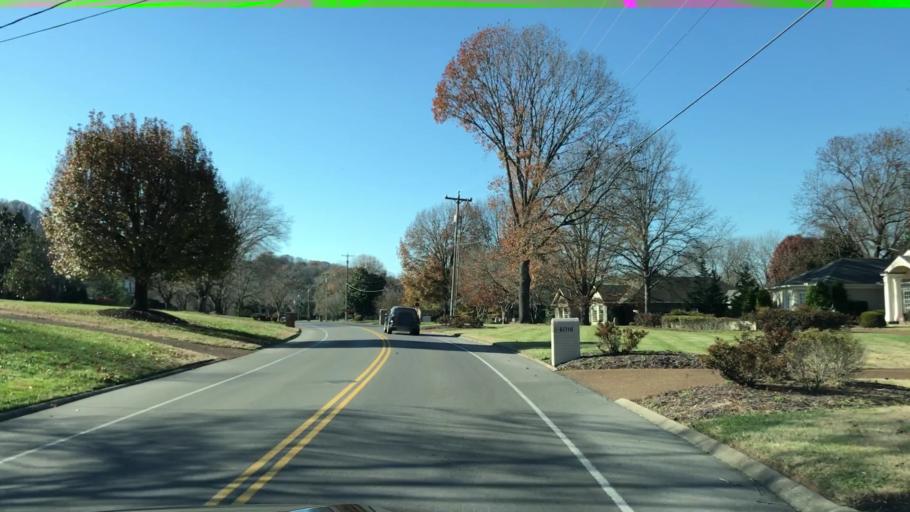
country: US
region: Tennessee
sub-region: Williamson County
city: Brentwood
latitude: 36.0258
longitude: -86.8233
